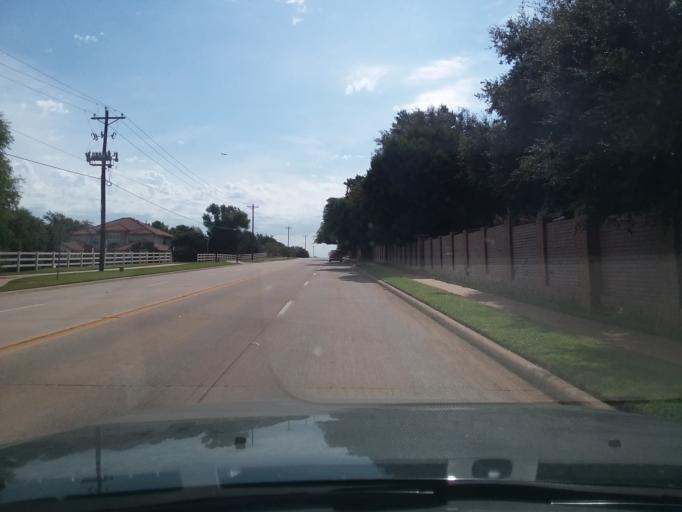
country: US
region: Texas
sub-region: Denton County
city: Flower Mound
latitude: 33.0138
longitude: -97.0876
